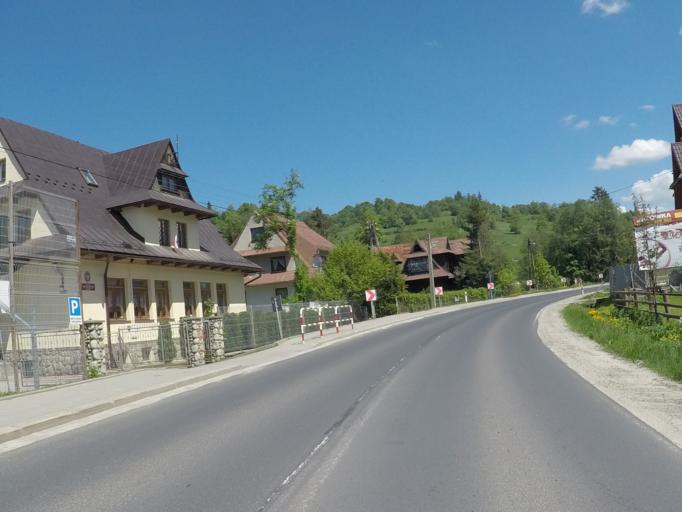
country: PL
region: Lesser Poland Voivodeship
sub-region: Powiat tatrzanski
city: Bukowina Tatrzanska
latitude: 49.3372
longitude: 20.0597
